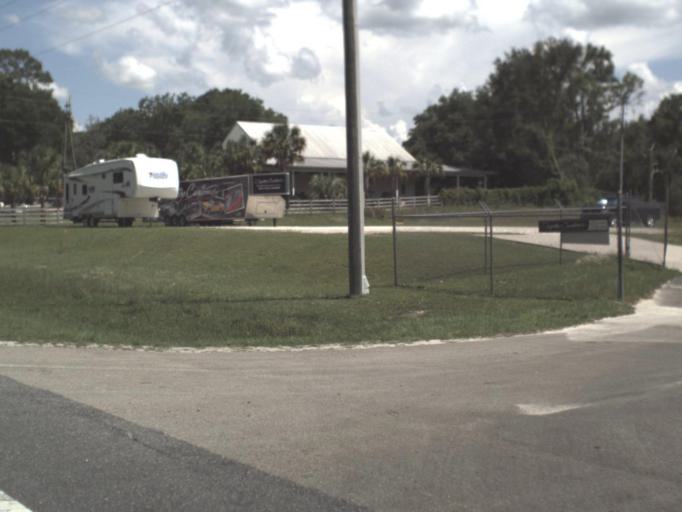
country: US
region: Florida
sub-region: Alachua County
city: High Springs
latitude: 29.8360
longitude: -82.6174
